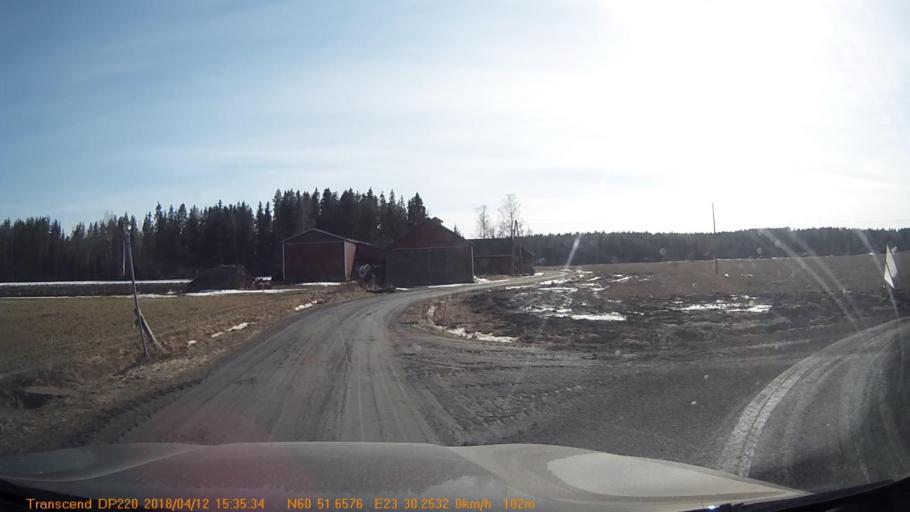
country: FI
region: Haeme
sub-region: Forssa
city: Jokioinen
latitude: 60.8610
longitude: 23.5042
